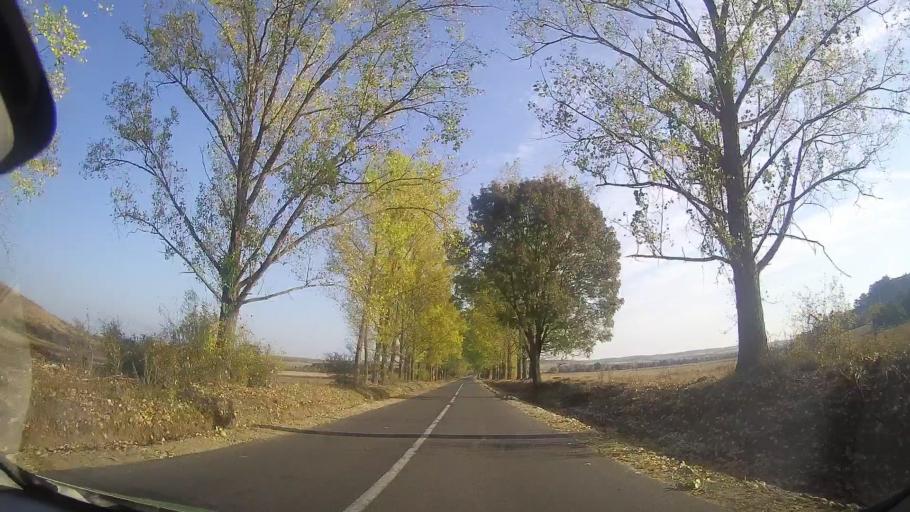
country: RO
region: Timis
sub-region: Comuna Masloc
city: Masloc
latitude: 45.9684
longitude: 21.4920
